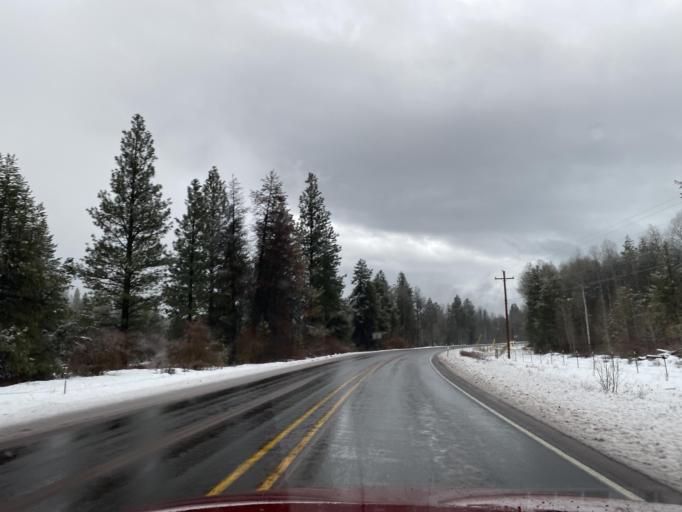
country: US
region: Oregon
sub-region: Klamath County
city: Klamath Falls
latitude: 42.4387
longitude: -122.1184
